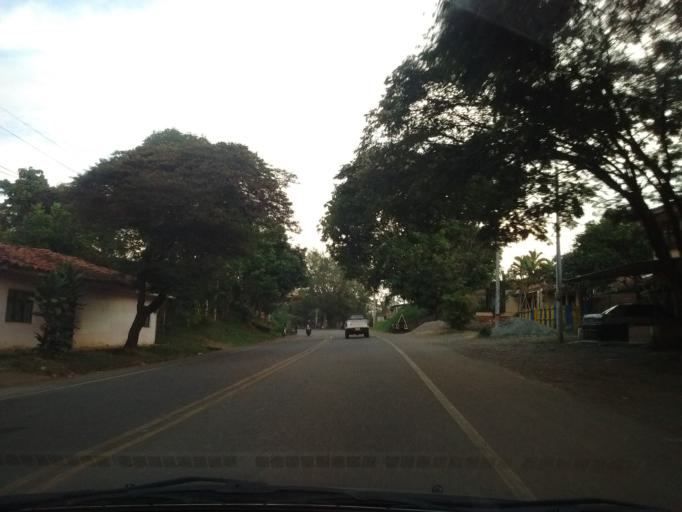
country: CO
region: Cauca
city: Santander de Quilichao
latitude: 2.9986
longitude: -76.4938
